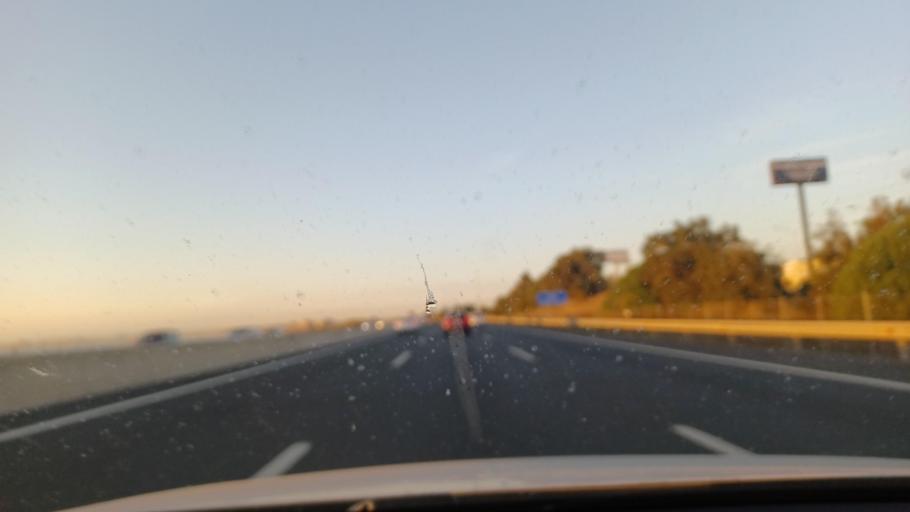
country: ES
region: Valencia
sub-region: Provincia de Valencia
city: Albuixech
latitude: 39.5370
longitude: -0.3074
